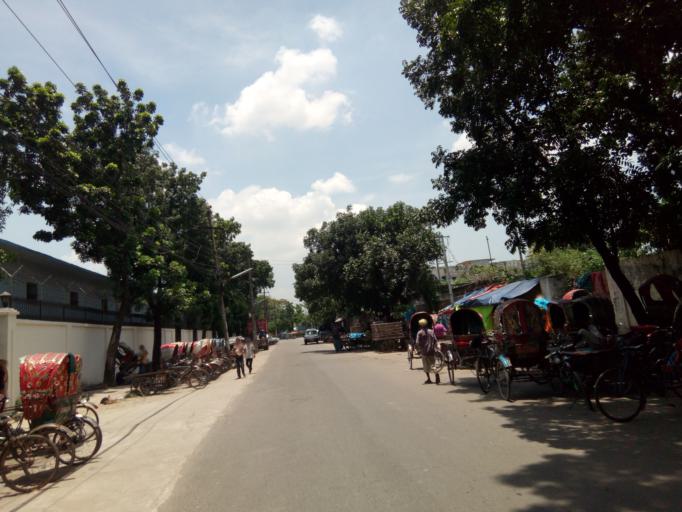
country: BD
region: Dhaka
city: Paltan
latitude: 23.7622
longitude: 90.4013
